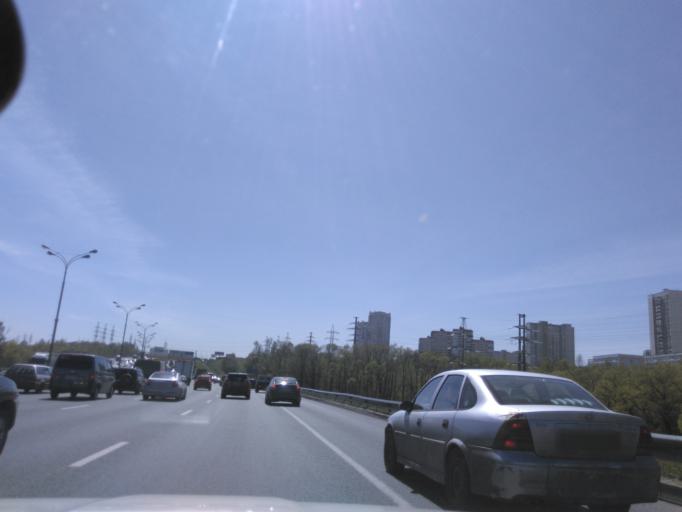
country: RU
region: Moscow
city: Strogino
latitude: 55.8450
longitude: 37.3919
